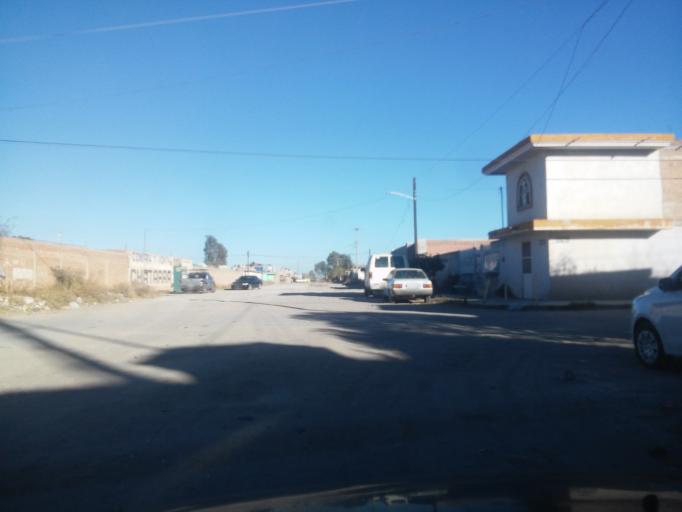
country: MX
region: Durango
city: Victoria de Durango
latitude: 24.0158
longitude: -104.6377
